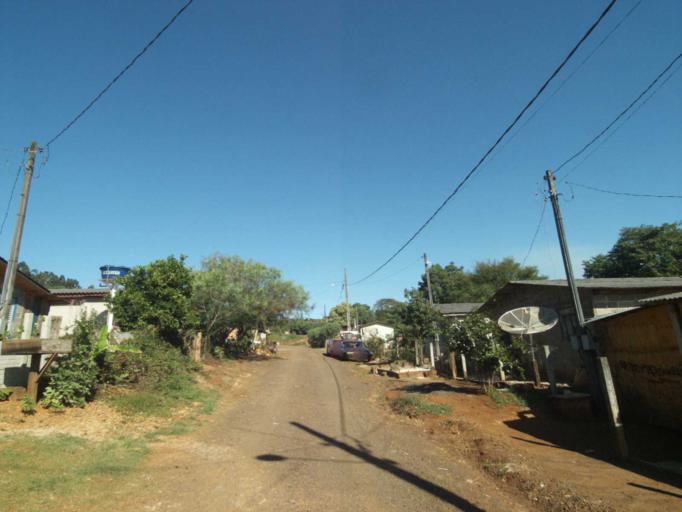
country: BR
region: Parana
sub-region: Laranjeiras Do Sul
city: Laranjeiras do Sul
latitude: -25.3792
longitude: -52.1975
